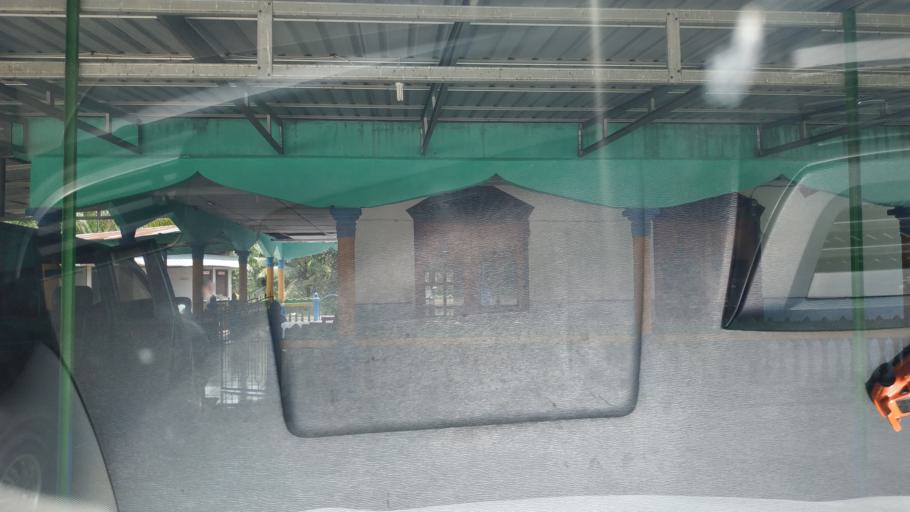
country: ID
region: North Sumatra
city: Langgapayung
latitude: 1.6113
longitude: 99.8700
